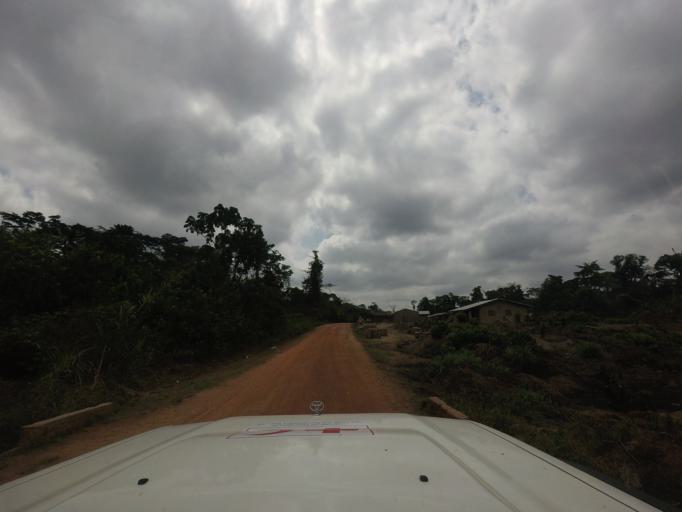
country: LR
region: Lofa
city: Voinjama
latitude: 8.4119
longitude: -9.7195
